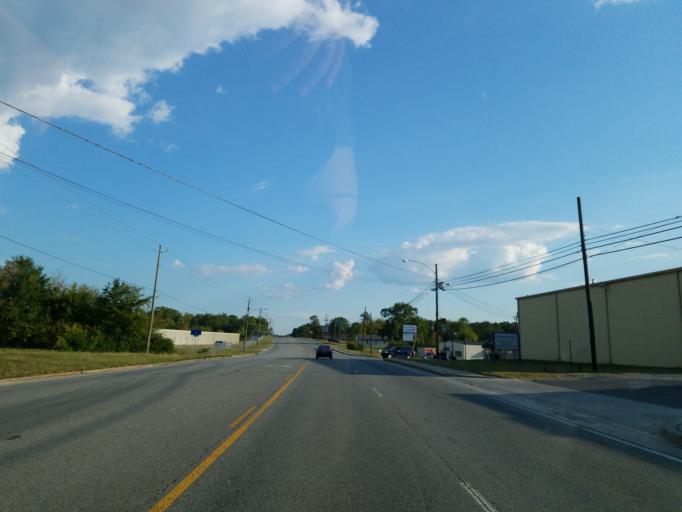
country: US
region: Georgia
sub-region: Murray County
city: Chatsworth
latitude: 34.7526
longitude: -84.7687
